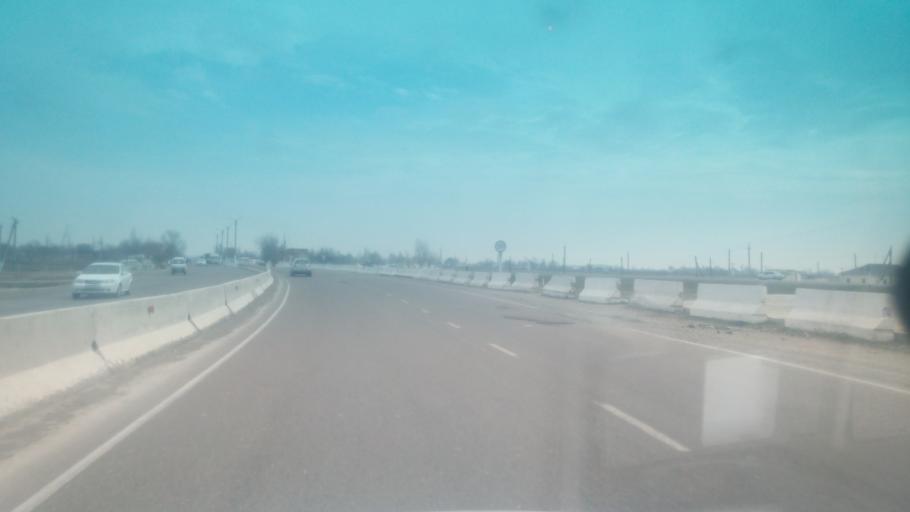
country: KZ
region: Ongtustik Qazaqstan
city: Myrzakent
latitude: 40.5040
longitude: 68.5203
